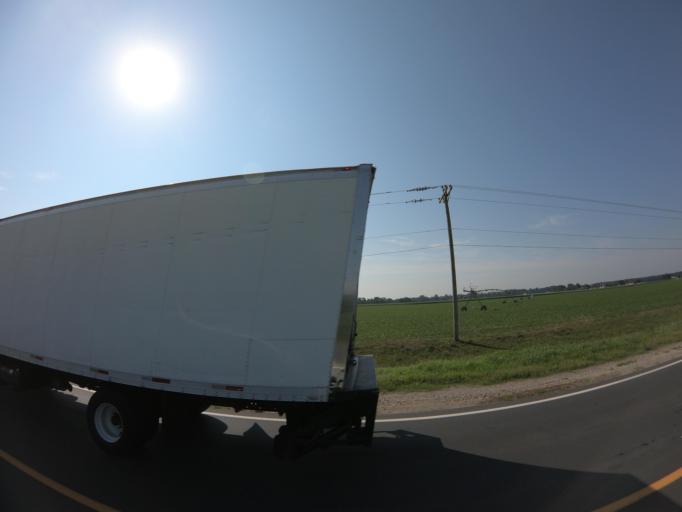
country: US
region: Delaware
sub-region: Sussex County
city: Bridgeville
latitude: 38.7582
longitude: -75.6212
